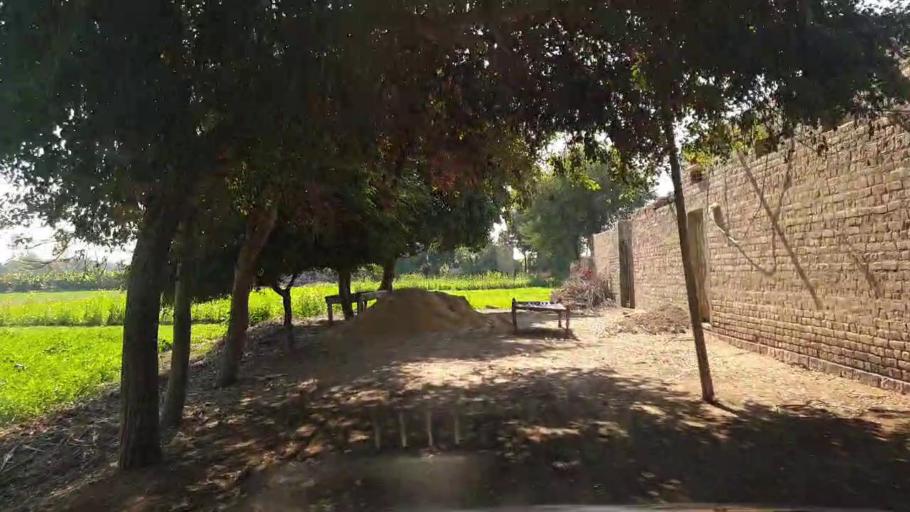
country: PK
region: Sindh
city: Shahdadpur
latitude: 25.9235
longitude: 68.5741
